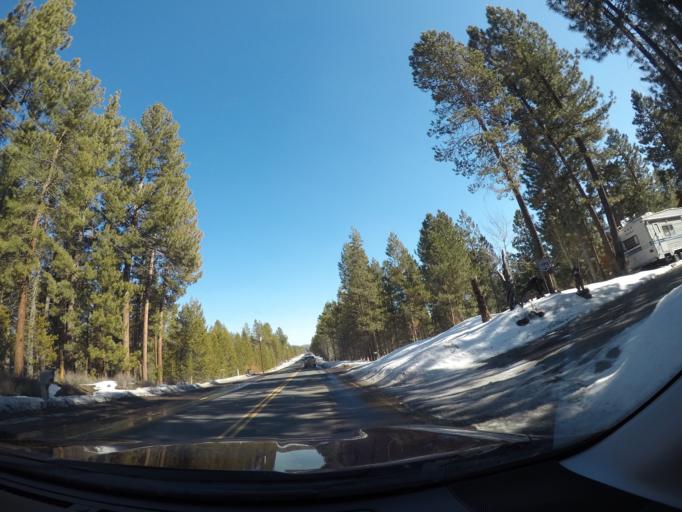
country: US
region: Oregon
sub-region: Deschutes County
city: Sunriver
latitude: 43.8629
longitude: -121.4734
